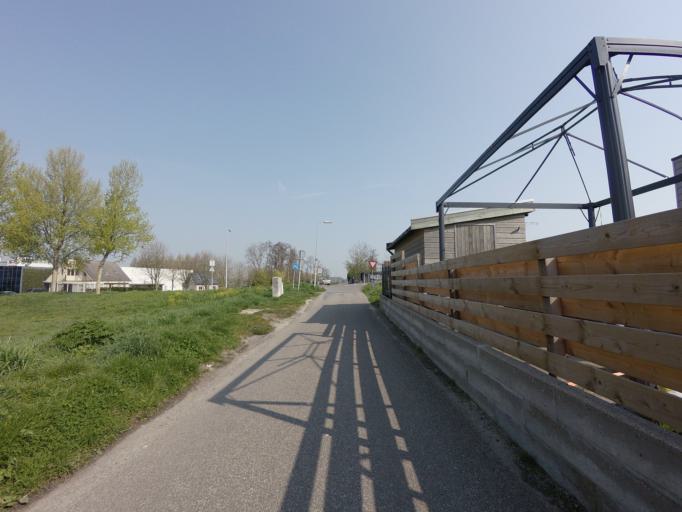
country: NL
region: South Holland
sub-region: Gemeente Gouda
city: Bloemendaal
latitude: 51.9922
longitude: 4.6731
